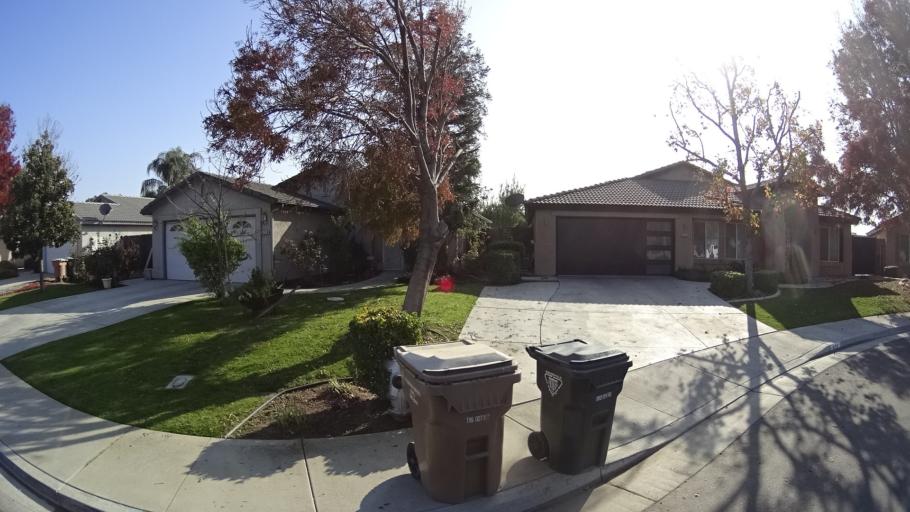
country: US
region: California
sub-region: Kern County
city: Greenacres
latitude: 35.3954
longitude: -119.0707
